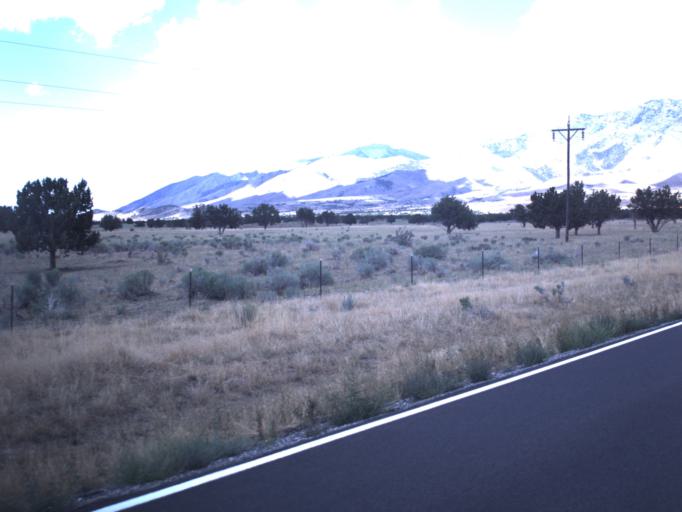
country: US
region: Utah
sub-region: Tooele County
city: Grantsville
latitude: 40.3057
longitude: -112.6432
